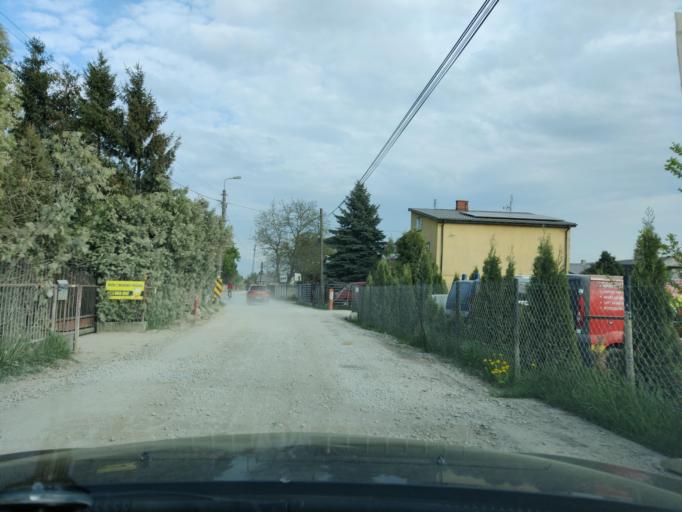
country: PL
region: Masovian Voivodeship
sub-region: Powiat piaseczynski
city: Konstancin-Jeziorna
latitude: 52.1240
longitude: 21.1459
